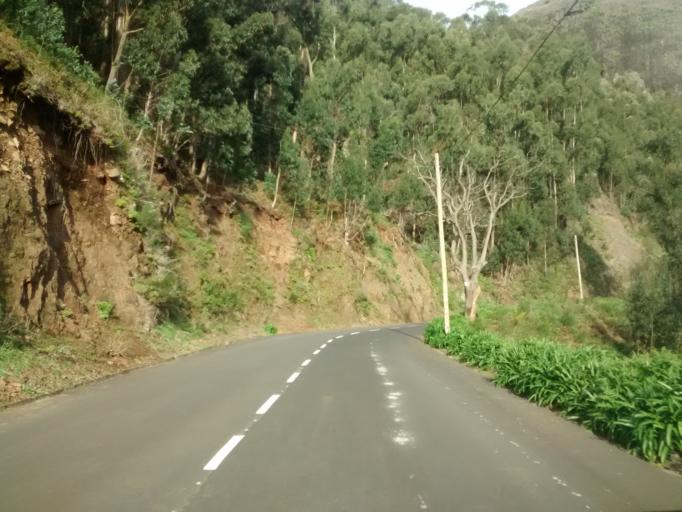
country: PT
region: Madeira
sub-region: Camara de Lobos
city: Curral das Freiras
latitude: 32.7395
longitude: -17.0251
